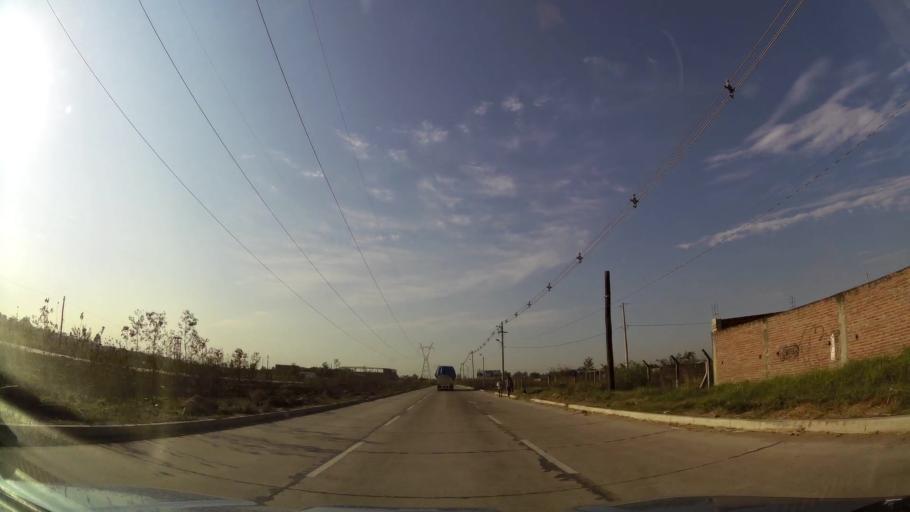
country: BO
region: Santa Cruz
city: Santa Cruz de la Sierra
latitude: -17.6888
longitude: -63.1444
